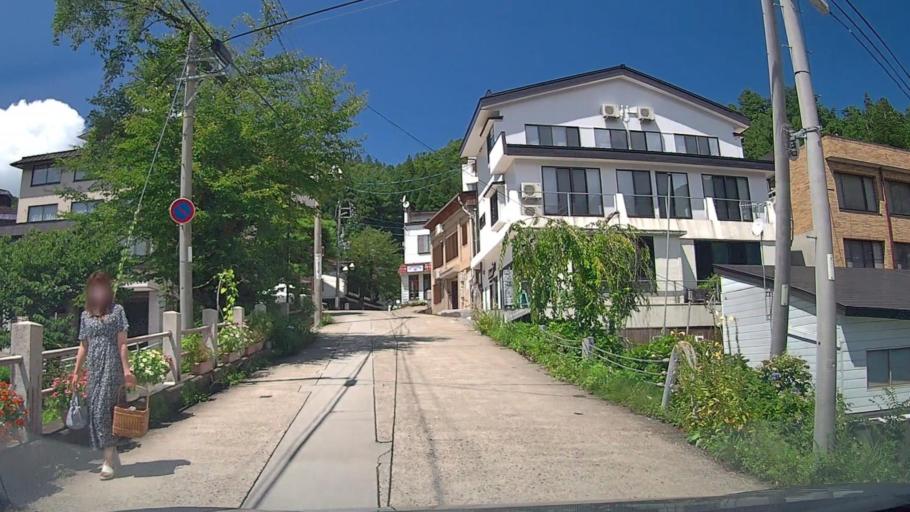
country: JP
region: Nagano
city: Iiyama
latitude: 36.9244
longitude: 138.4461
